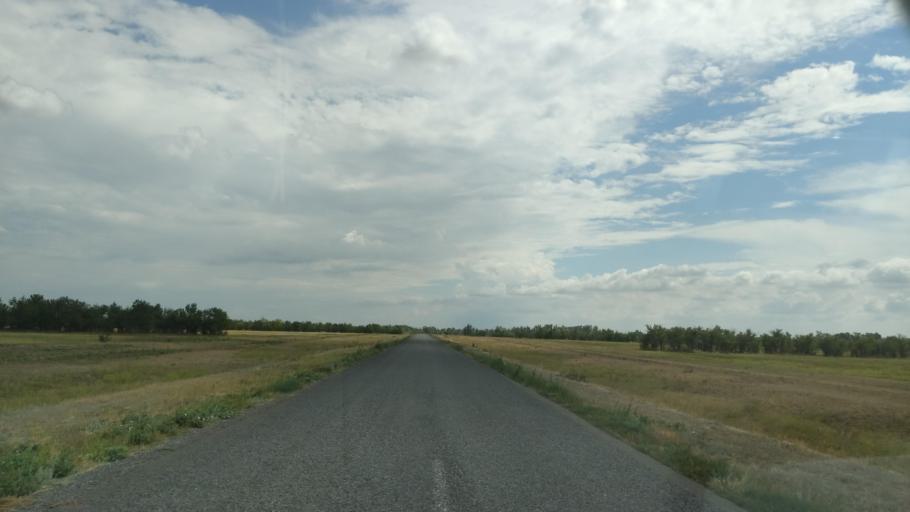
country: KZ
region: Pavlodar
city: Pavlodar
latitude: 52.6367
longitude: 76.9781
